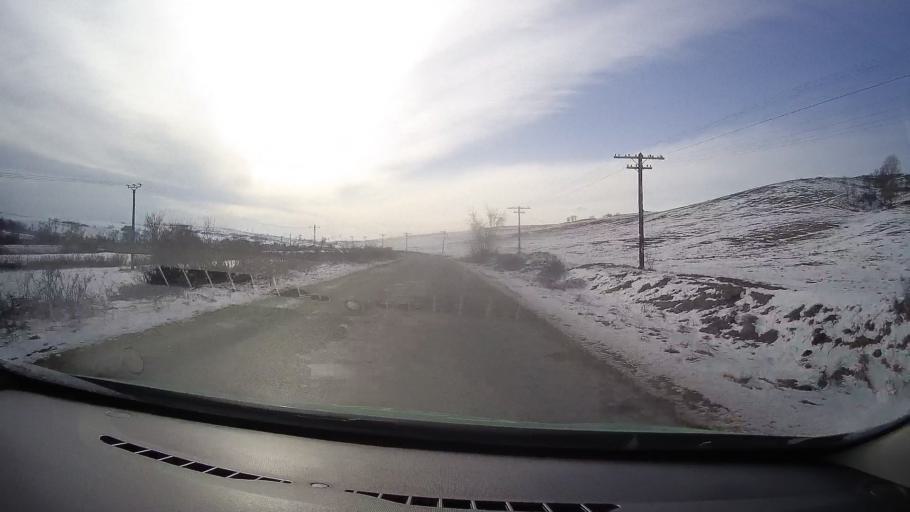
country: RO
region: Sibiu
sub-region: Oras Agnita
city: Ruja
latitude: 45.9947
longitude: 24.6663
